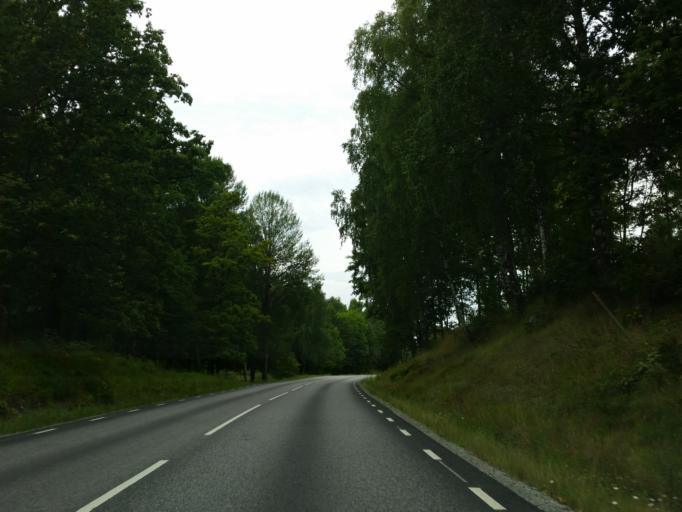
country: SE
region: Stockholm
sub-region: Salems Kommun
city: Ronninge
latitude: 59.2303
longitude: 17.7160
